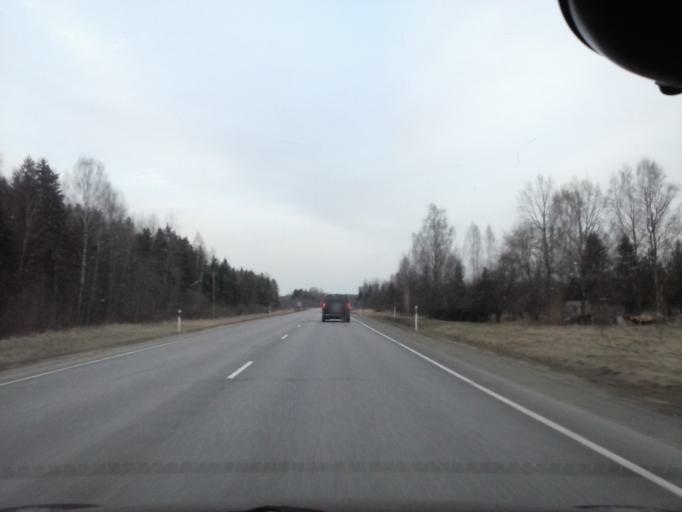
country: EE
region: Tartu
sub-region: Puhja vald
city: Puhja
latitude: 58.5198
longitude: 26.3145
